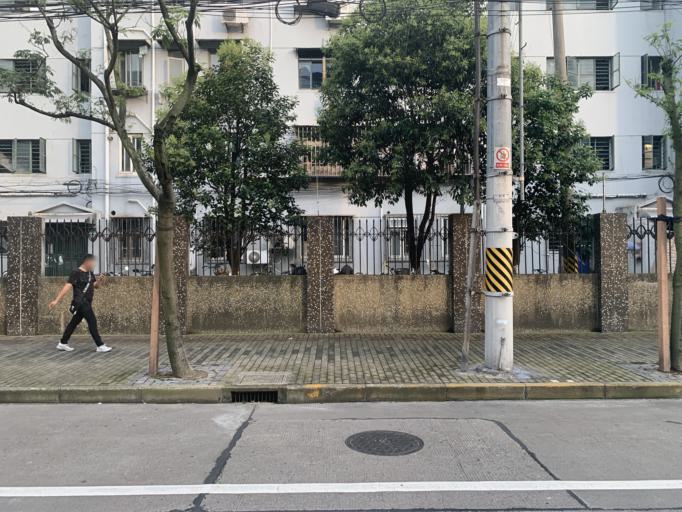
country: CN
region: Shanghai Shi
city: Huamu
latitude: 31.2451
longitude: 121.5693
